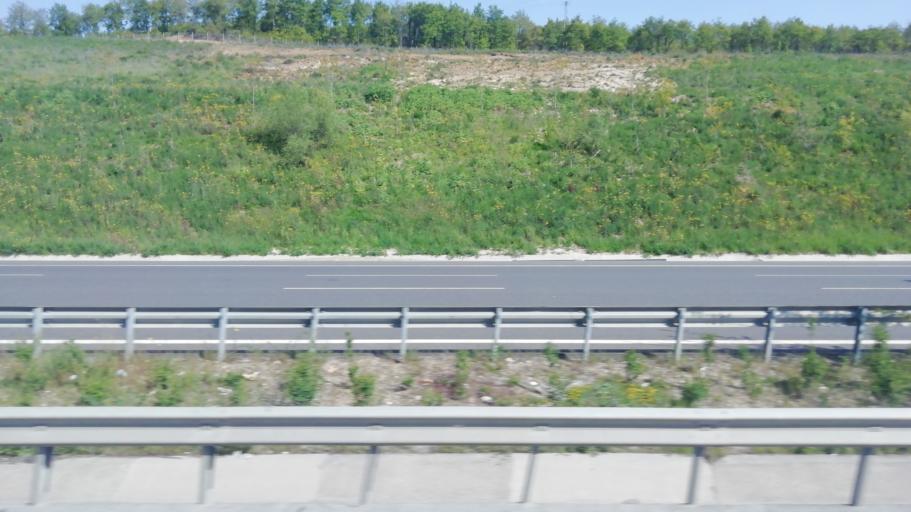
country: TR
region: Istanbul
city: Kemerburgaz
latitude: 41.2300
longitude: 28.8630
